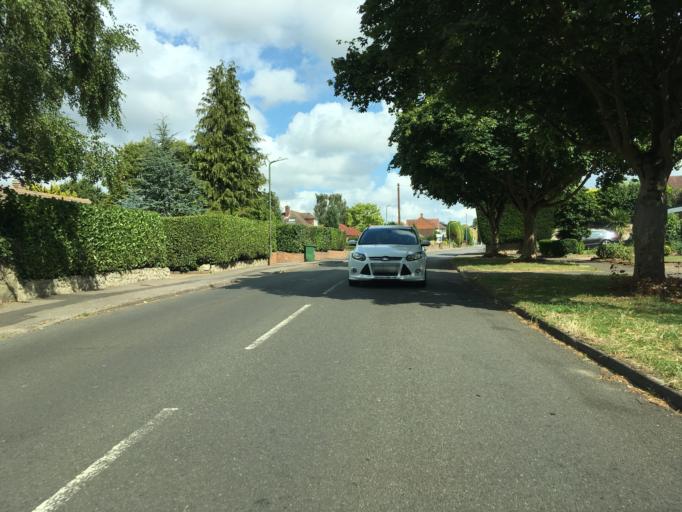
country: GB
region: England
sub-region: Kent
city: Maidstone
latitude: 51.2532
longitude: 0.5238
